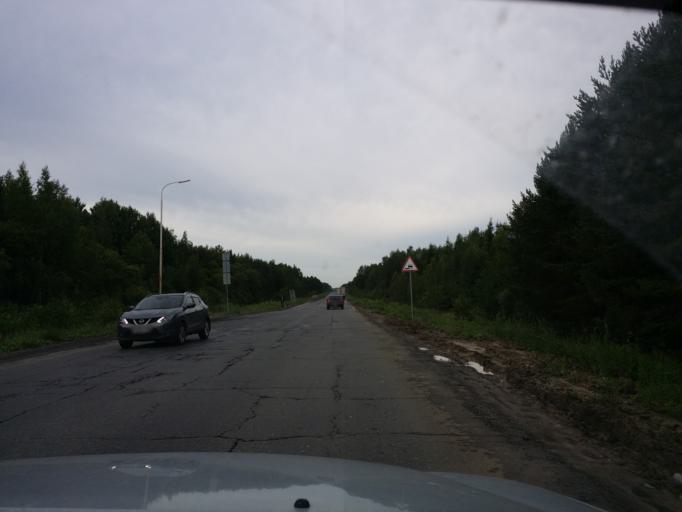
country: RU
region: Tjumen
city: Turtas
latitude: 58.6725
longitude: 68.8196
